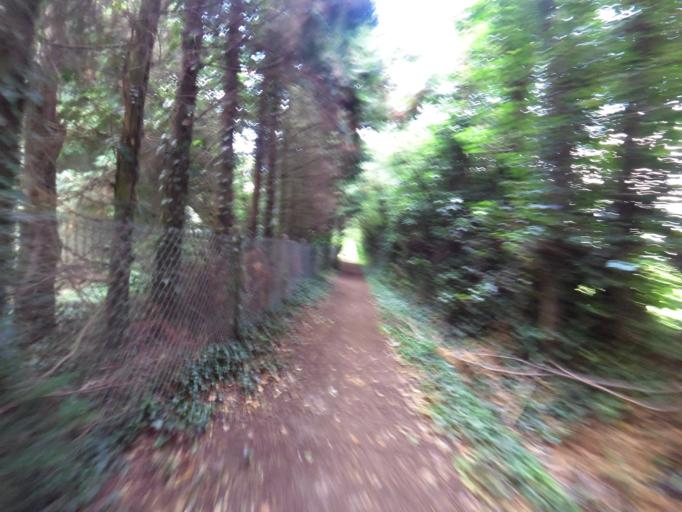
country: GB
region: England
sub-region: Suffolk
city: Ipswich
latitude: 52.0728
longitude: 1.1545
